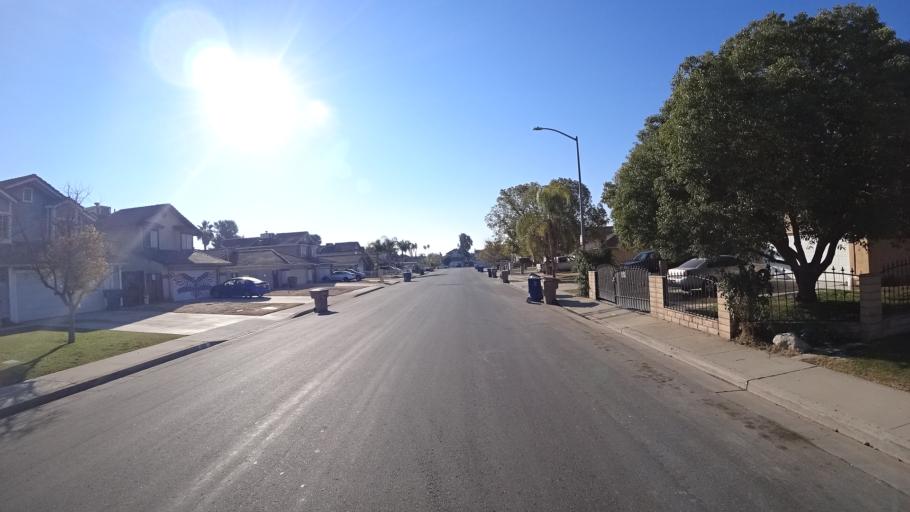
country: US
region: California
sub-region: Kern County
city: Greenfield
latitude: 35.3065
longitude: -119.0193
